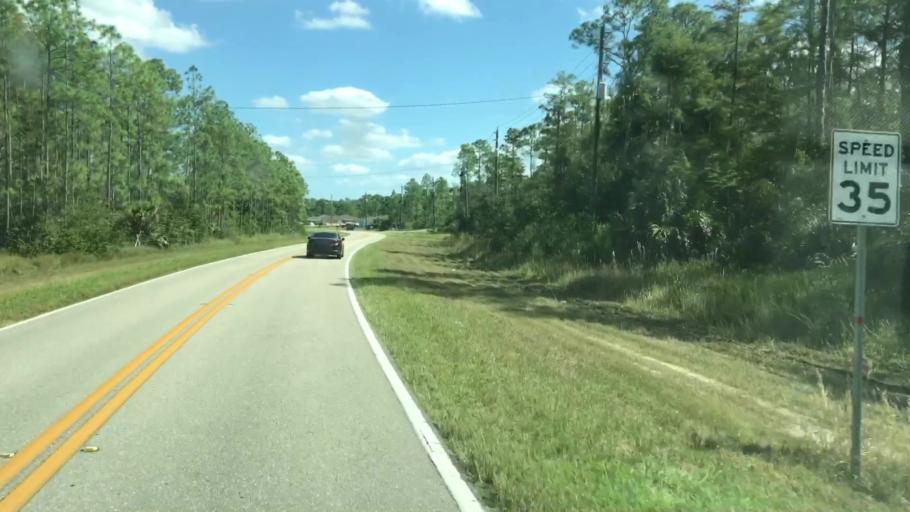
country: US
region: Florida
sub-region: Lee County
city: Alva
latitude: 26.6772
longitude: -81.6037
